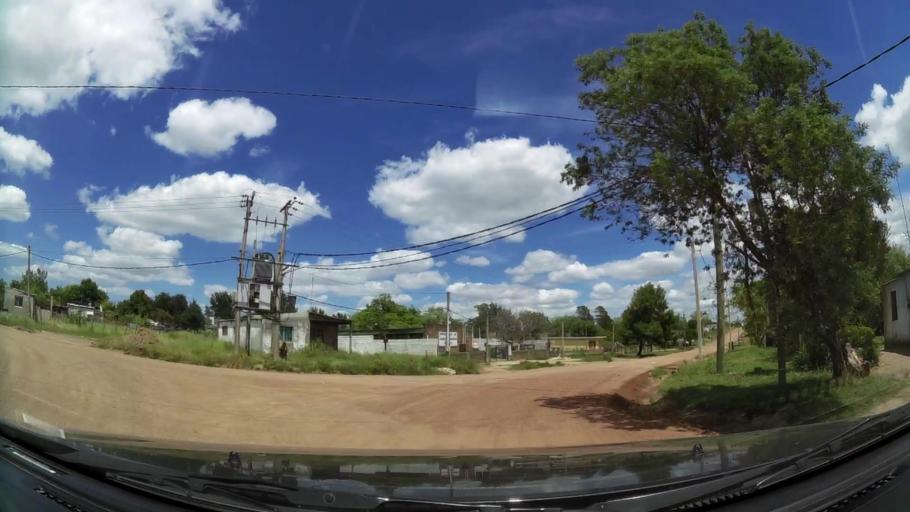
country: UY
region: Canelones
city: Colonia Nicolich
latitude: -34.7937
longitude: -55.9927
